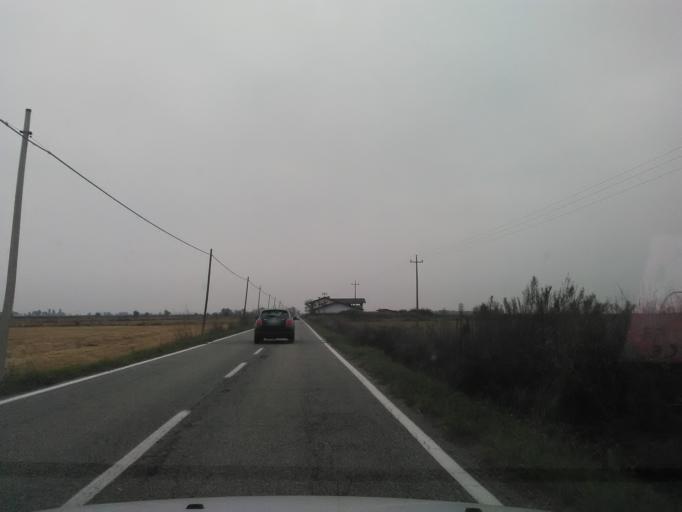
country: IT
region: Piedmont
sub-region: Provincia di Vercelli
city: Bianze
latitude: 45.2755
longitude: 8.1208
